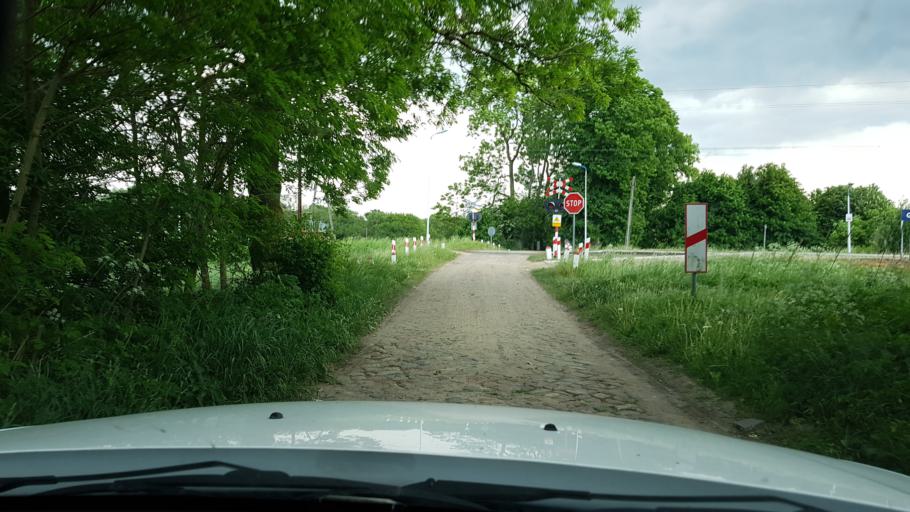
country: PL
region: West Pomeranian Voivodeship
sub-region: Powiat stargardzki
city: Stara Dabrowa
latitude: 53.3730
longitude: 15.1769
